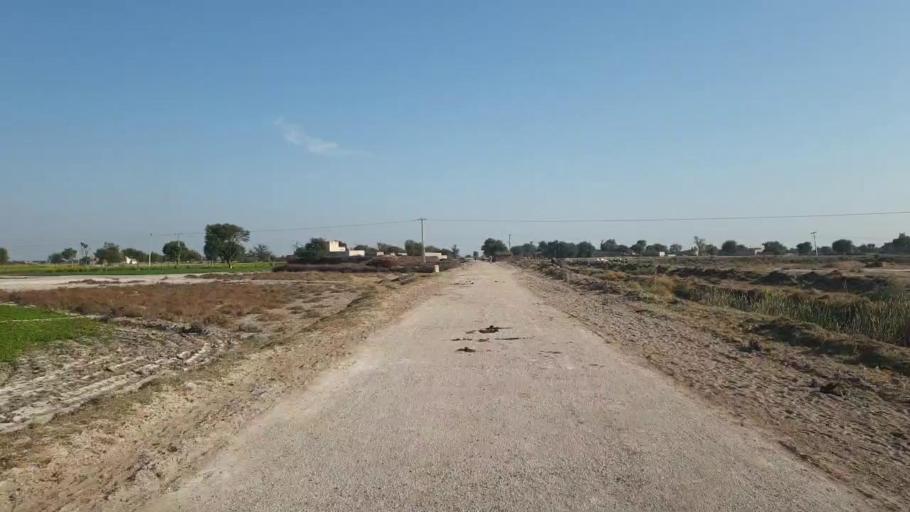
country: PK
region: Sindh
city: Shahpur Chakar
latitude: 26.1680
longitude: 68.6609
